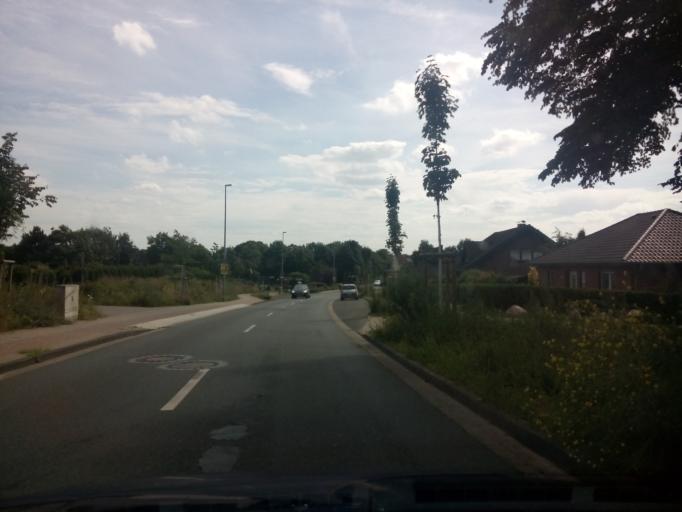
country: DE
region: Lower Saxony
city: Osterholz-Scharmbeck
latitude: 53.2301
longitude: 8.7990
